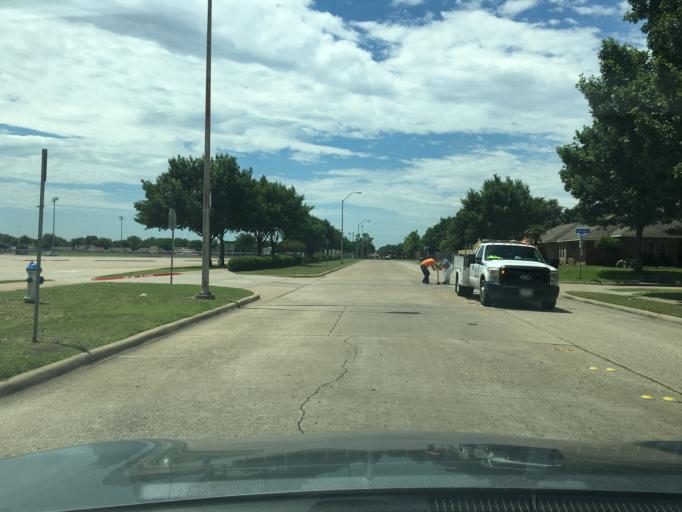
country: US
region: Texas
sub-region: Dallas County
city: Richardson
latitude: 32.9375
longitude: -96.6952
